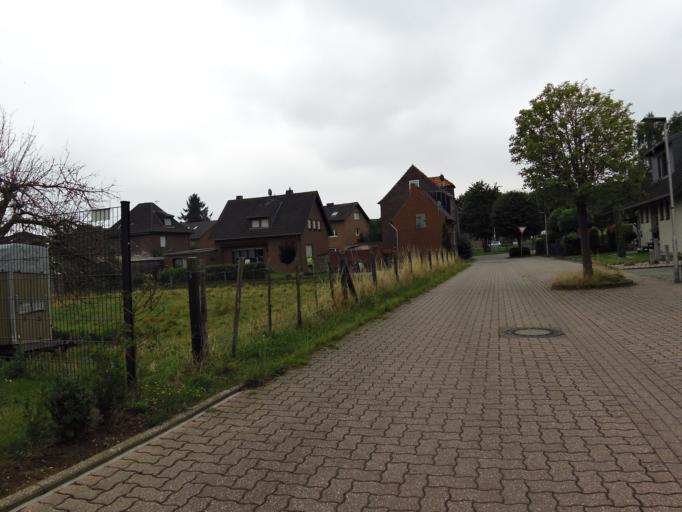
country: DE
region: North Rhine-Westphalia
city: Geilenkirchen
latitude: 50.9943
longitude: 6.1858
